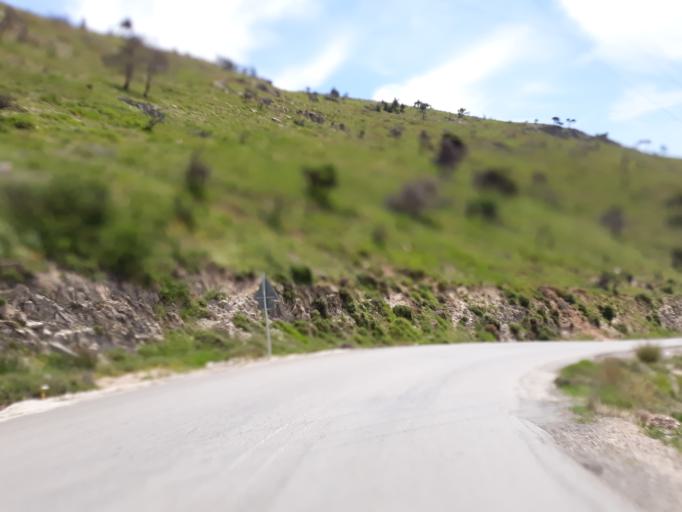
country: GR
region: Attica
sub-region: Nomarchia Dytikis Attikis
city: Magoula
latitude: 38.1630
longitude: 23.5393
